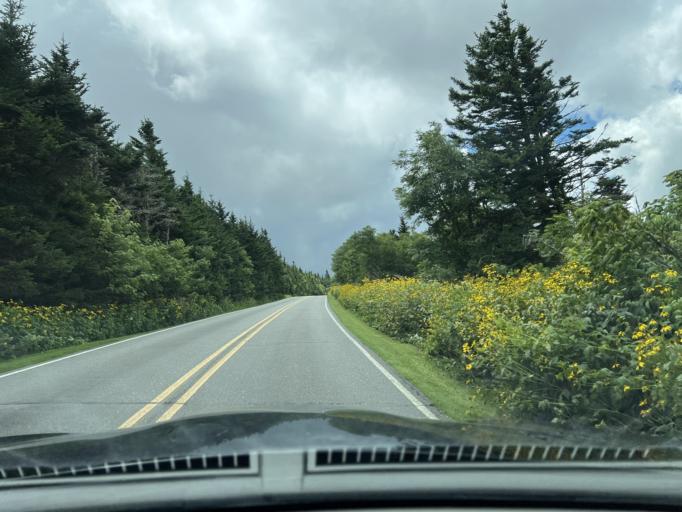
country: US
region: North Carolina
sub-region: Buncombe County
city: Black Mountain
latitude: 35.7564
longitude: -82.2722
